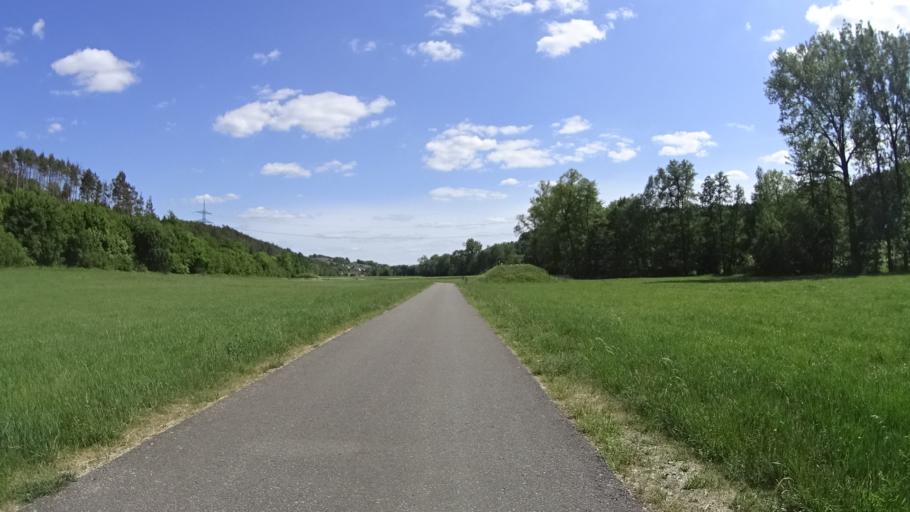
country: DE
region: Baden-Wuerttemberg
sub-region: Karlsruhe Region
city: Hardheim
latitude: 49.5940
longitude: 9.4799
